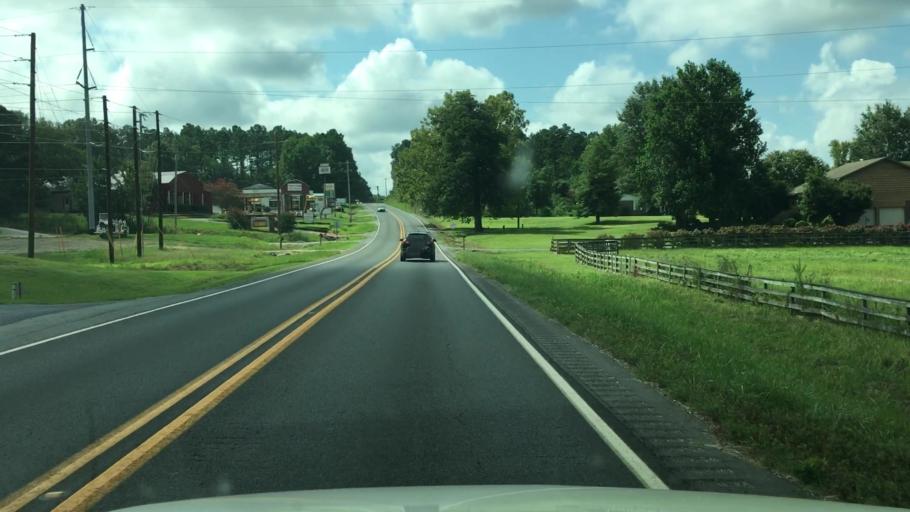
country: US
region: Arkansas
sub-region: Garland County
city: Lake Hamilton
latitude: 34.3144
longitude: -93.1702
